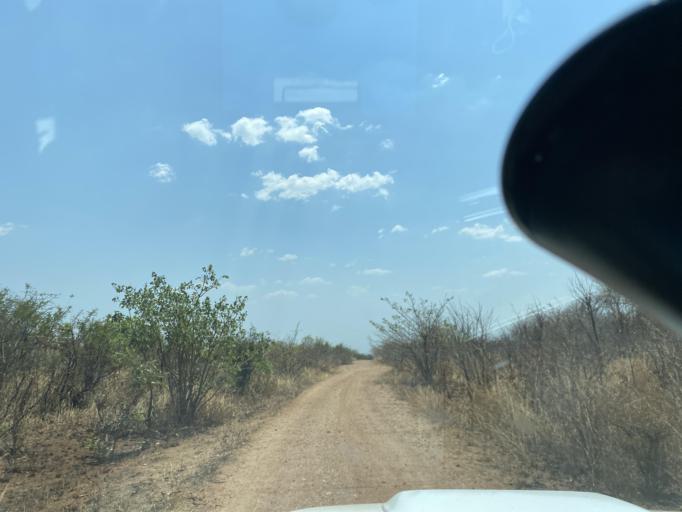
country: ZM
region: Lusaka
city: Lusaka
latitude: -15.5063
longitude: 27.9730
